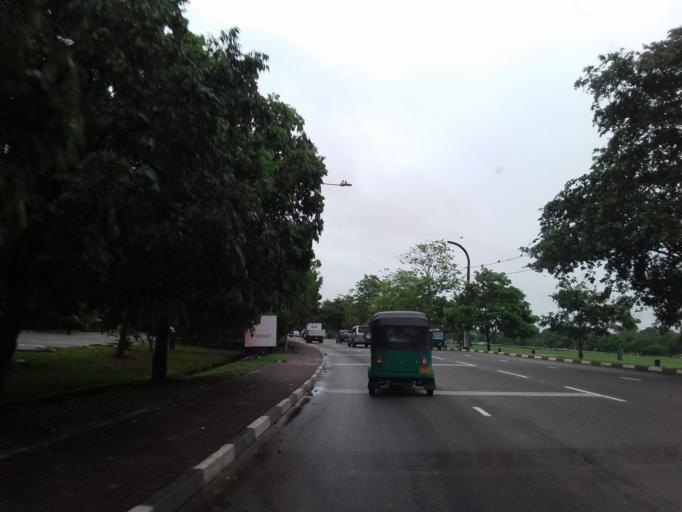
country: LK
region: Western
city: Battaramulla South
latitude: 6.8936
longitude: 79.9174
